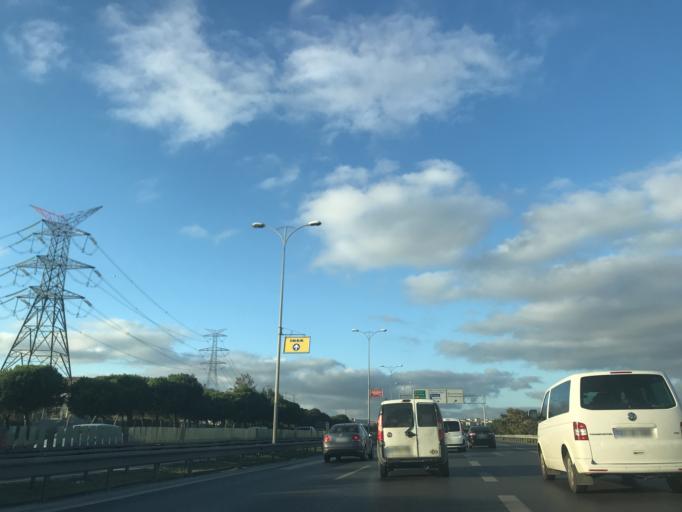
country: TR
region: Istanbul
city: Esenler
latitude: 41.0517
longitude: 28.8857
